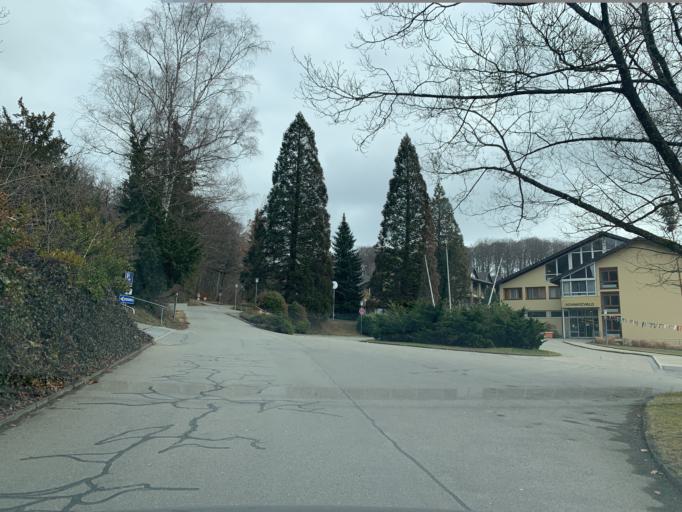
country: DE
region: Baden-Wuerttemberg
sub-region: Freiburg Region
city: Gailingen
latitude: 47.7031
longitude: 8.7531
